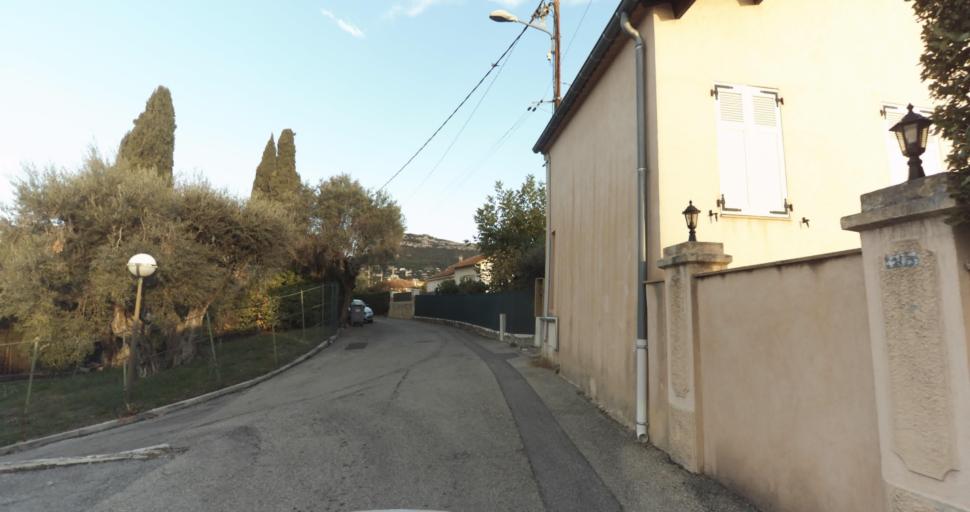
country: FR
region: Provence-Alpes-Cote d'Azur
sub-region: Departement des Alpes-Maritimes
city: Vence
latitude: 43.7178
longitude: 7.1229
